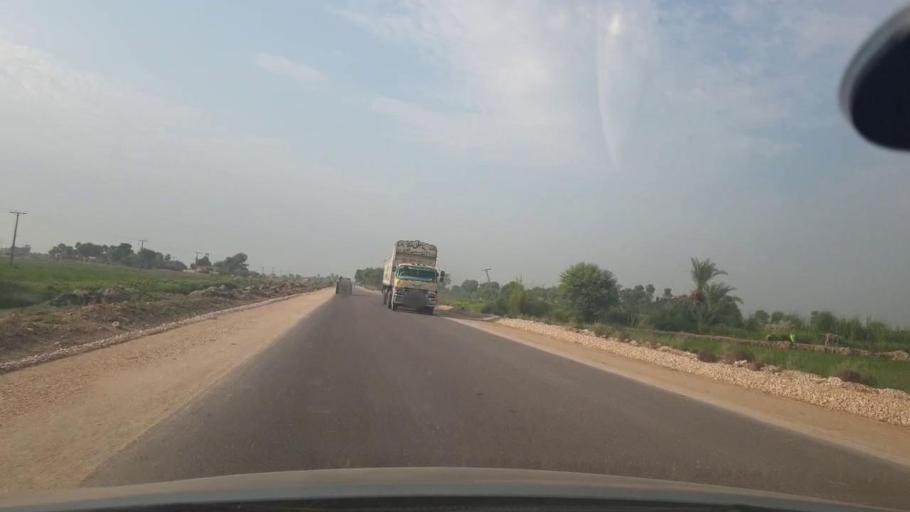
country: PK
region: Sindh
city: Jacobabad
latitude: 28.2025
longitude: 68.3680
